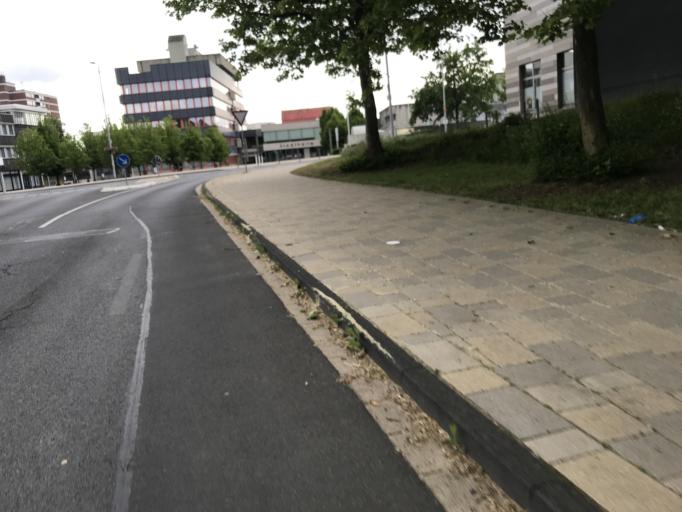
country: DE
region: Hesse
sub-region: Regierungsbezirk Kassel
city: Baunatal
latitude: 51.2563
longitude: 9.4130
